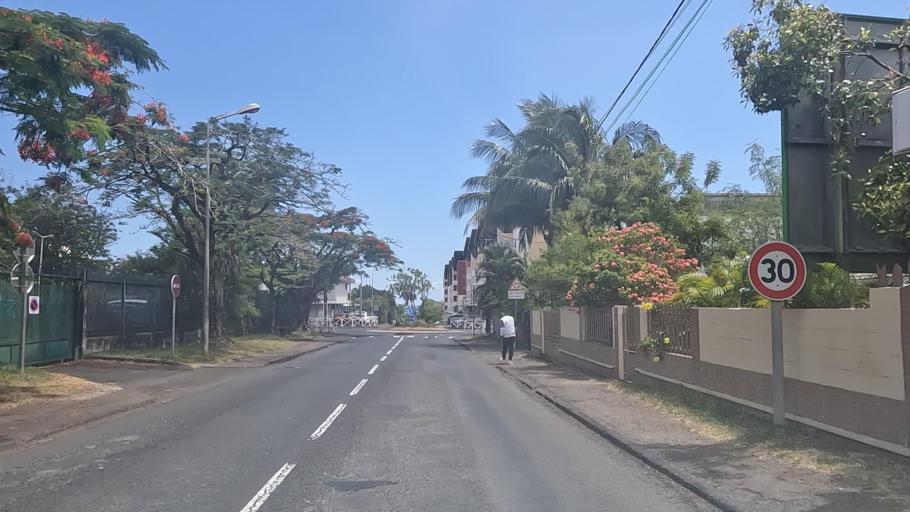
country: RE
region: Reunion
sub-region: Reunion
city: Saint-Benoit
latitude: -21.0332
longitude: 55.7082
